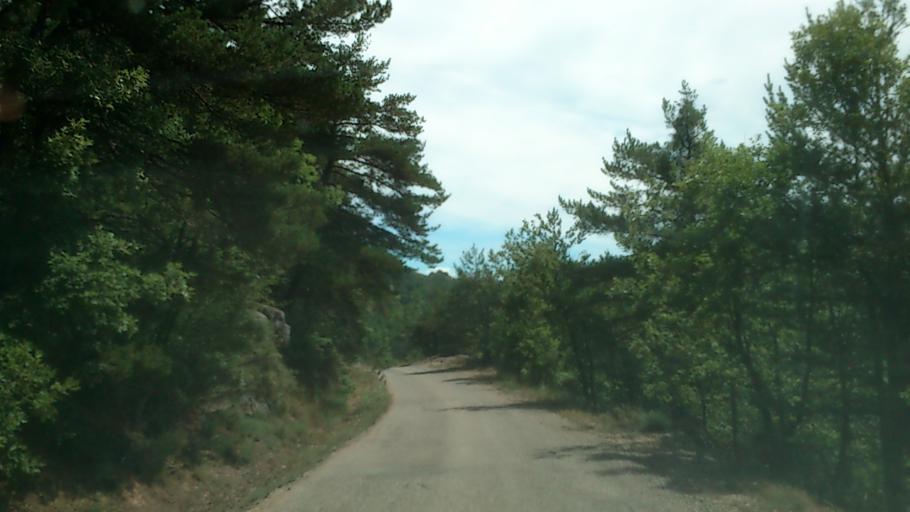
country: ES
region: Aragon
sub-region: Provincia de Huesca
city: Yebra de Basa
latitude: 42.3252
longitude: -0.2642
